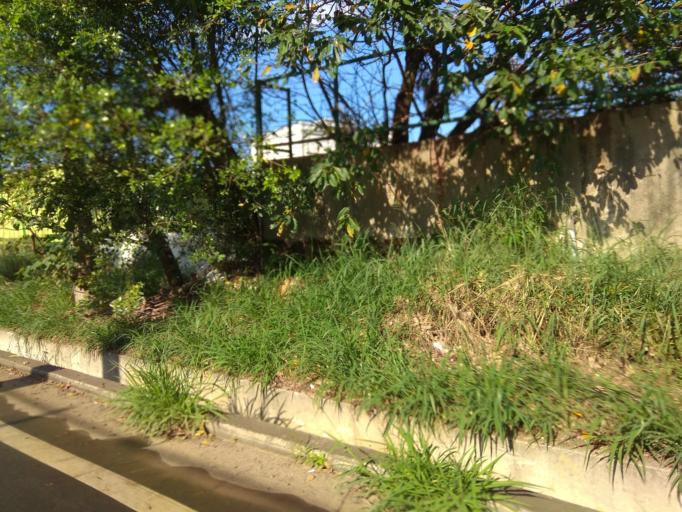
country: TW
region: Taiwan
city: Taoyuan City
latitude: 25.0695
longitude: 121.2039
